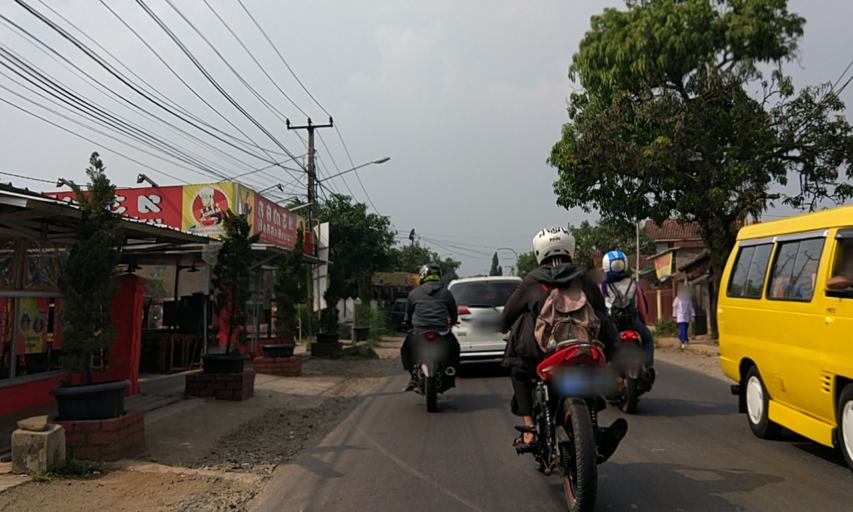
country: ID
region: West Java
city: Banjaran
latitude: -7.0522
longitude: 107.5751
